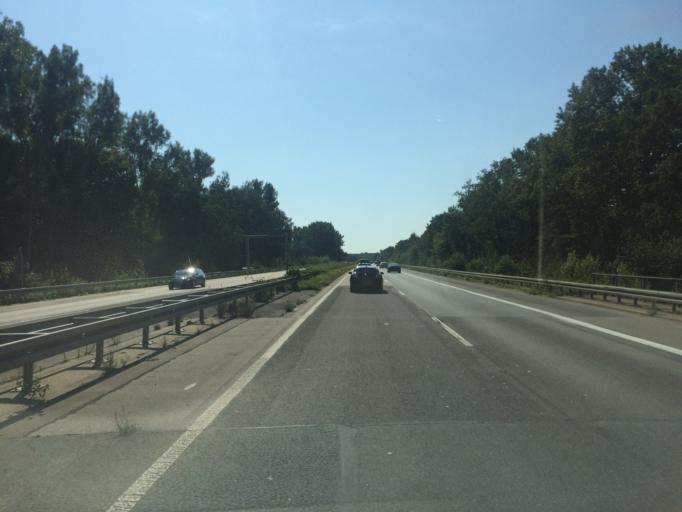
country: DE
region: North Rhine-Westphalia
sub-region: Regierungsbezirk Munster
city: Senden
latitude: 51.8754
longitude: 7.5762
